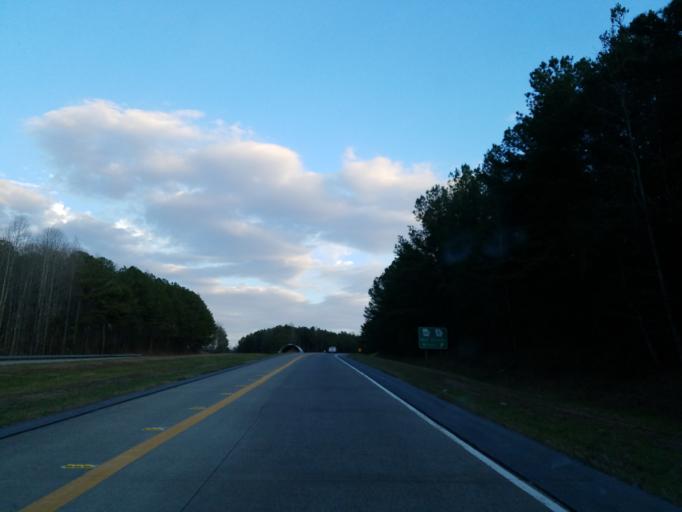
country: US
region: Georgia
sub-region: Pickens County
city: Nelson
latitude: 34.3725
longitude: -84.3795
